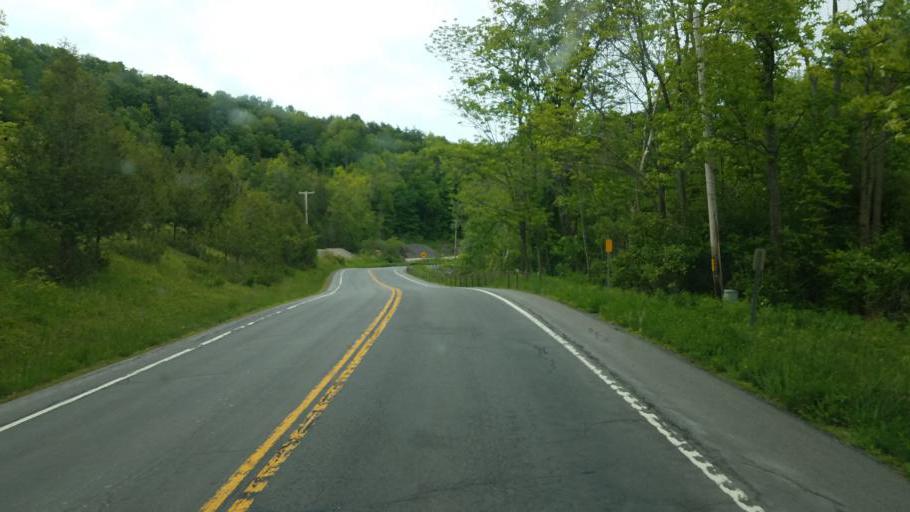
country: US
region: New York
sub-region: Herkimer County
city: Frankfort
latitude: 42.9668
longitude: -75.1009
